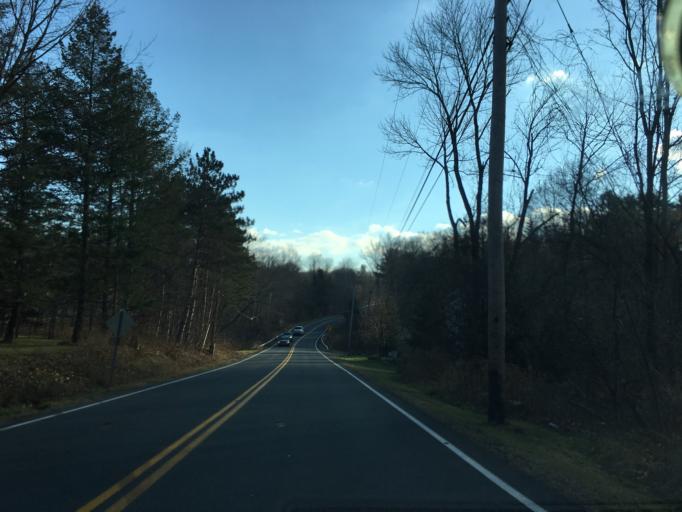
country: US
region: New York
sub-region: Rensselaer County
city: East Greenbush
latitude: 42.6304
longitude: -73.6652
